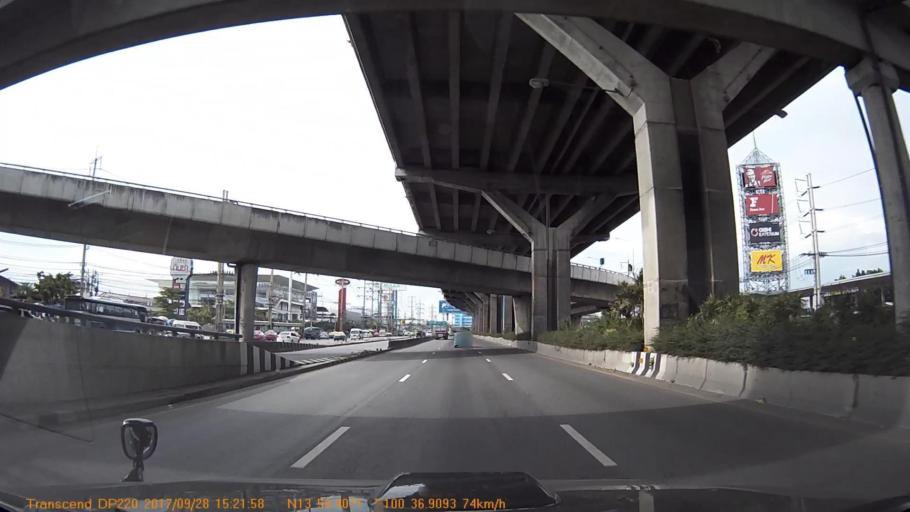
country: TH
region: Phra Nakhon Si Ayutthaya
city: Ban Bang Kadi Pathum Thani
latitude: 13.9904
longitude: 100.6151
